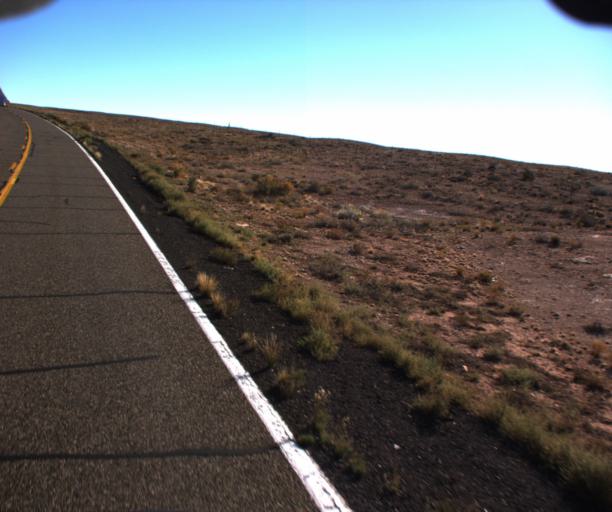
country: US
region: Arizona
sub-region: Coconino County
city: LeChee
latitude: 36.6885
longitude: -111.6553
